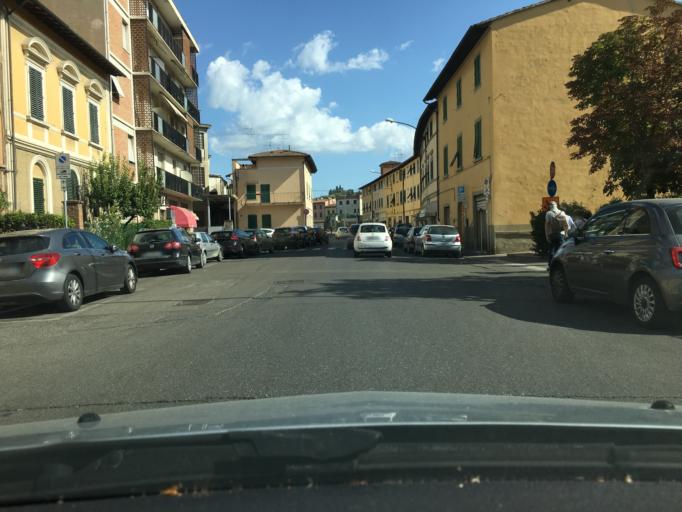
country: IT
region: Tuscany
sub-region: Province of Florence
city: Castelfiorentino
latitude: 43.6029
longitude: 10.9674
